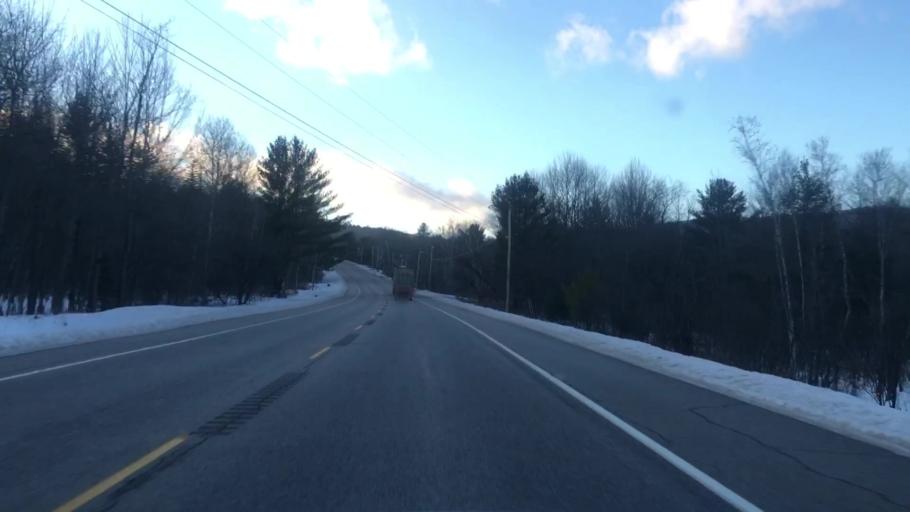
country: US
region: Maine
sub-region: Oxford County
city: Peru
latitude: 44.5872
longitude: -70.3473
